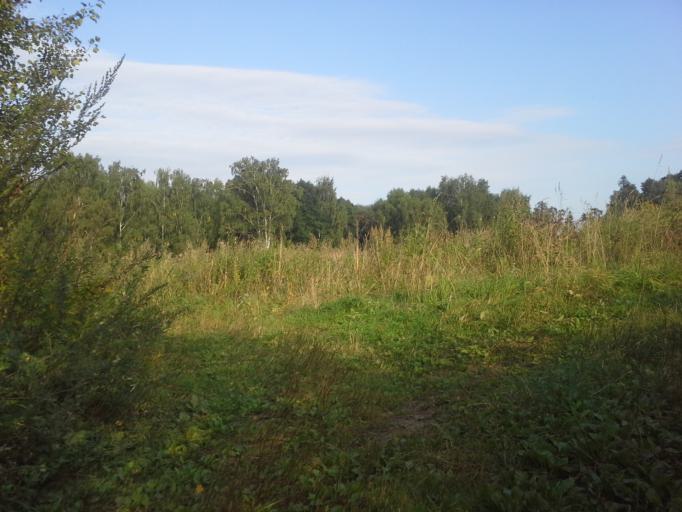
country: RU
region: Moskovskaya
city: Filimonki
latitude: 55.5469
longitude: 37.3388
